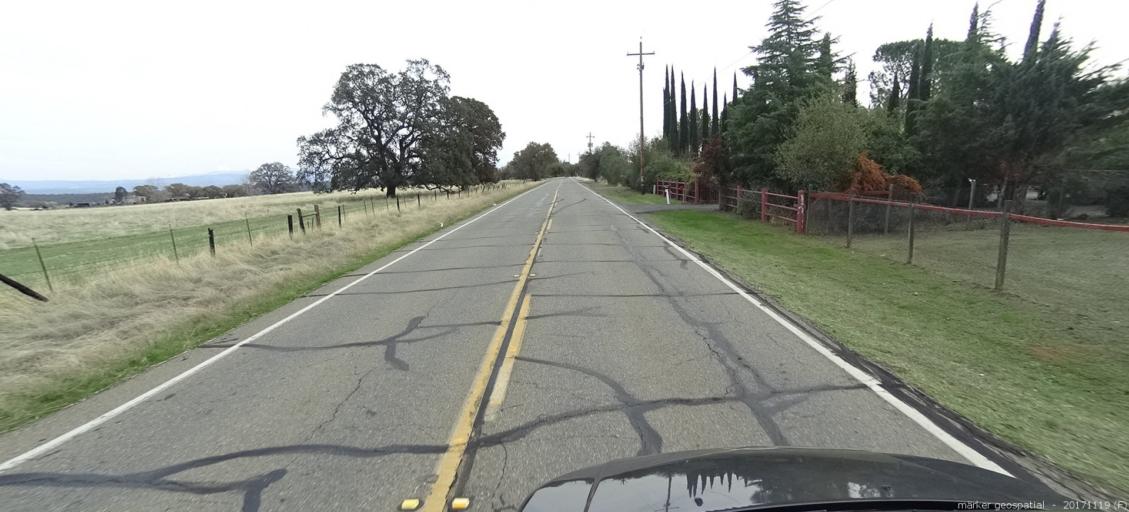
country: US
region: California
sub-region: Shasta County
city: Anderson
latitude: 40.4778
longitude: -122.2510
